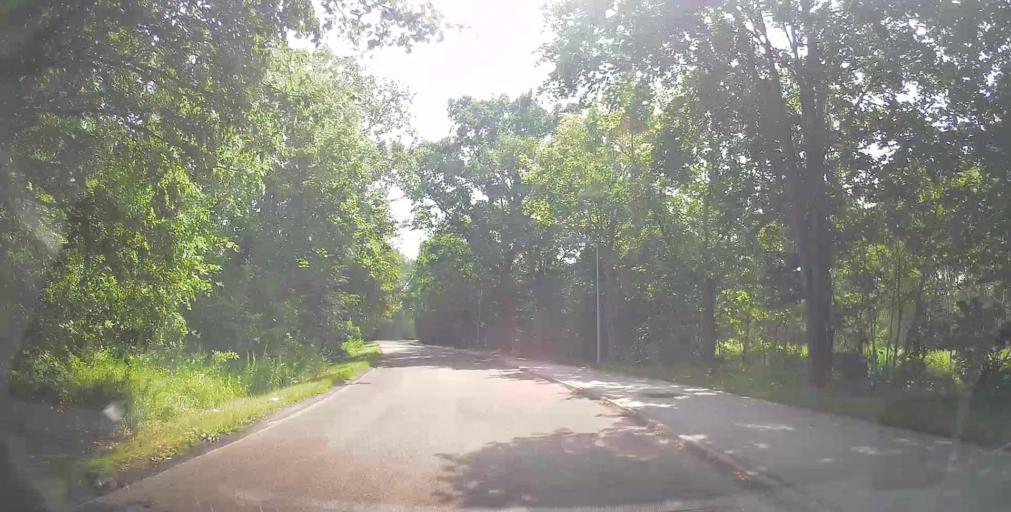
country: PL
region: Masovian Voivodeship
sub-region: Powiat bialobrzeski
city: Bialobrzegi
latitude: 51.6346
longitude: 20.9534
